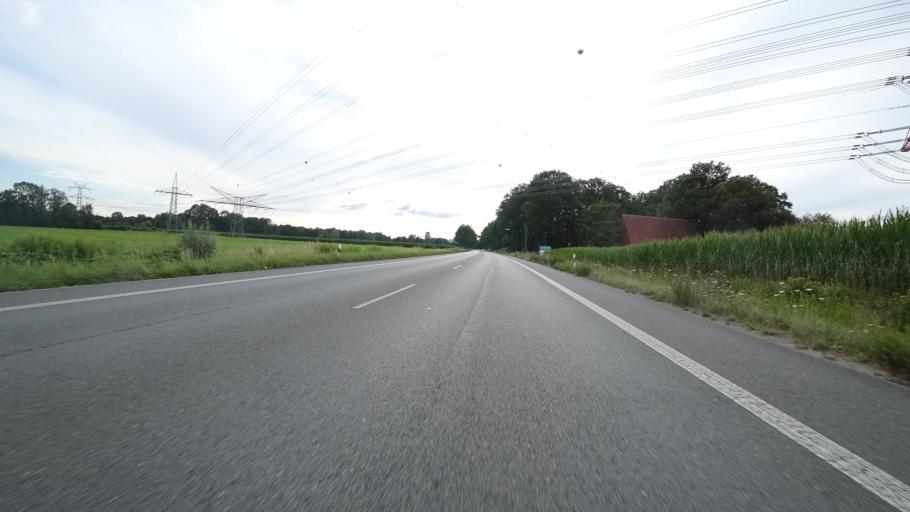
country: DE
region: North Rhine-Westphalia
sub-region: Regierungsbezirk Detmold
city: Guetersloh
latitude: 51.9211
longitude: 8.3495
